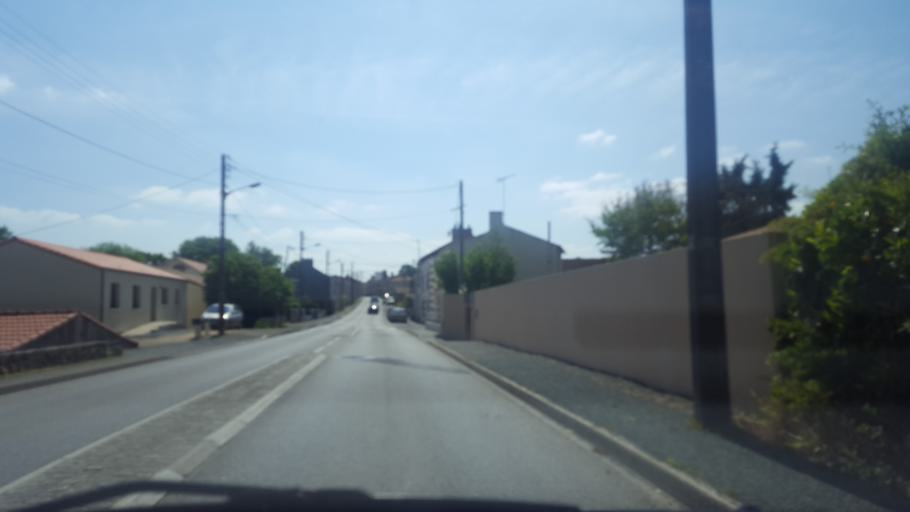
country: FR
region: Pays de la Loire
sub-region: Departement de la Loire-Atlantique
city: La Limouziniere
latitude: 47.0168
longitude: -1.5677
